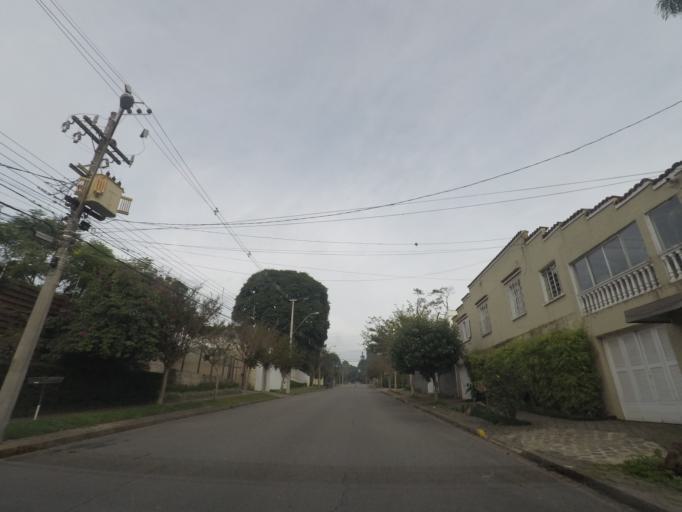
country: BR
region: Parana
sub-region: Curitiba
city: Curitiba
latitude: -25.4417
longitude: -49.2953
